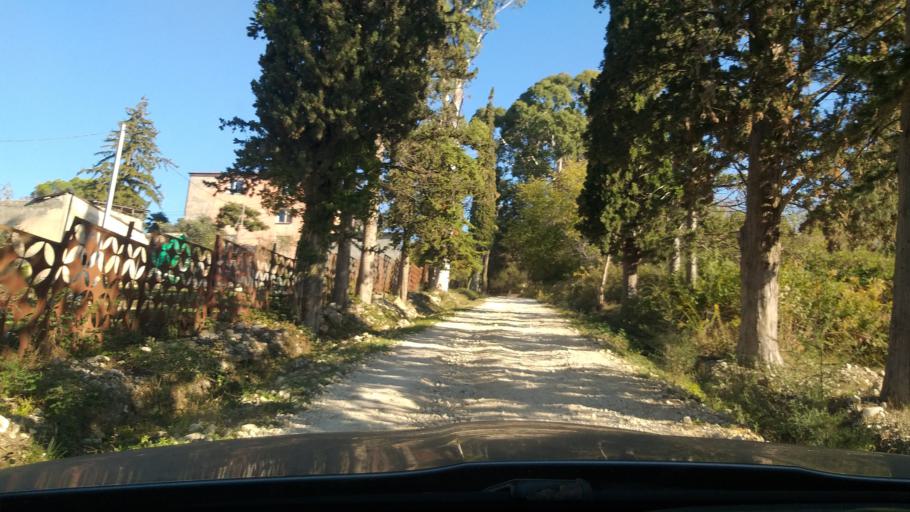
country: GE
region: Abkhazia
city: Stantsiya Novyy Afon
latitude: 43.0484
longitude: 40.8988
